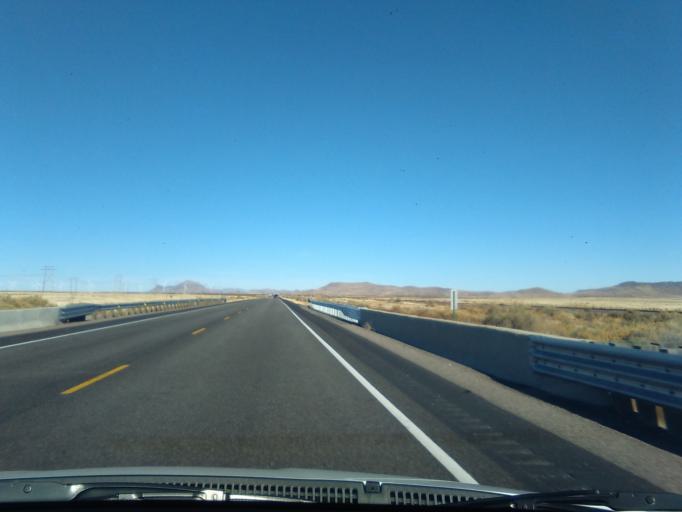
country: US
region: New Mexico
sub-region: Luna County
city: Deming
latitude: 32.4778
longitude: -107.5302
